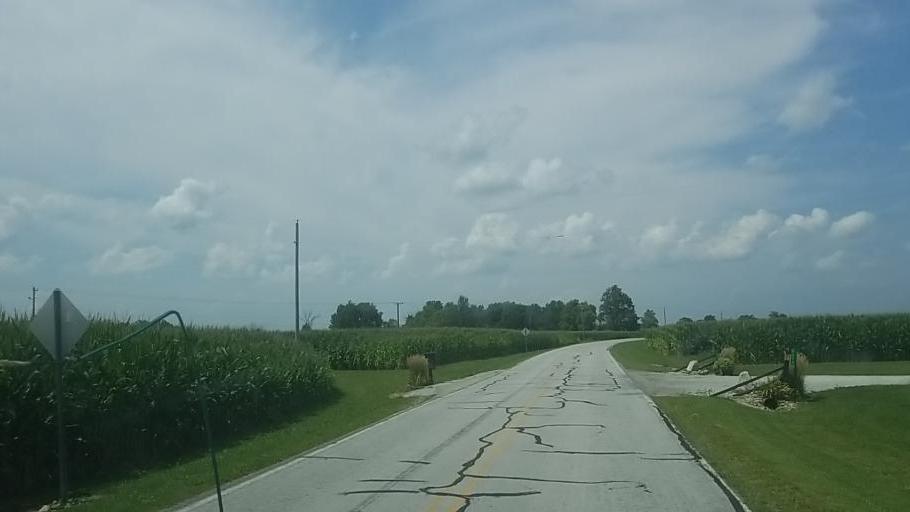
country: US
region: Ohio
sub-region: Hardin County
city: Kenton
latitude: 40.6936
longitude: -83.5747
